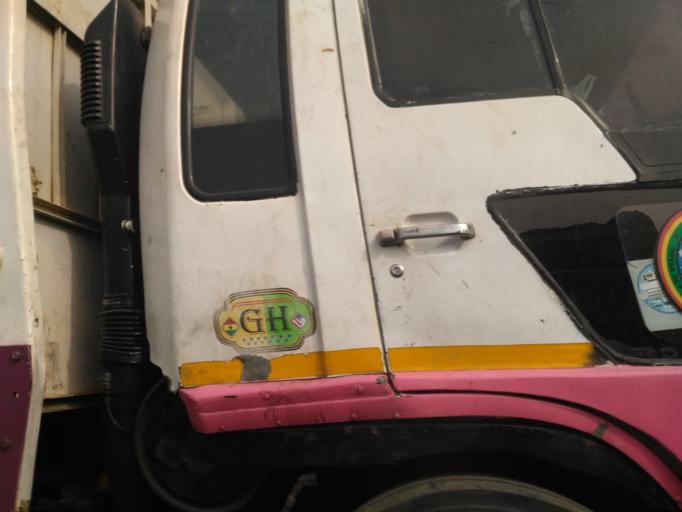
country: GH
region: Ashanti
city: Kumasi
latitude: 6.6978
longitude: -1.6136
